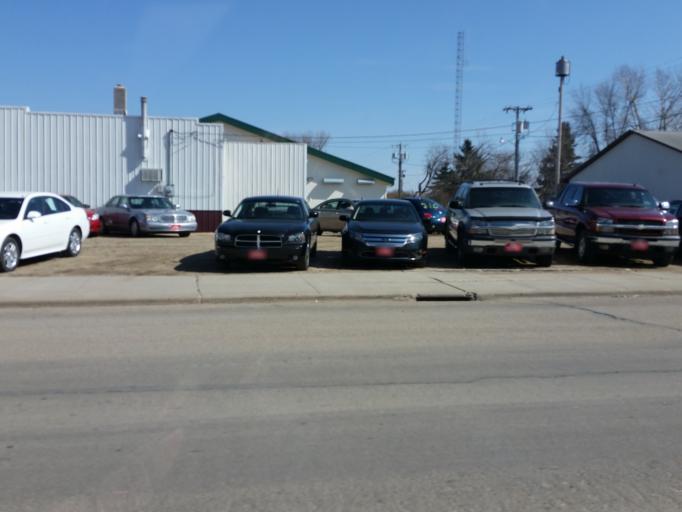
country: US
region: North Dakota
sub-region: Walsh County
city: Grafton
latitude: 48.2913
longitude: -97.3715
